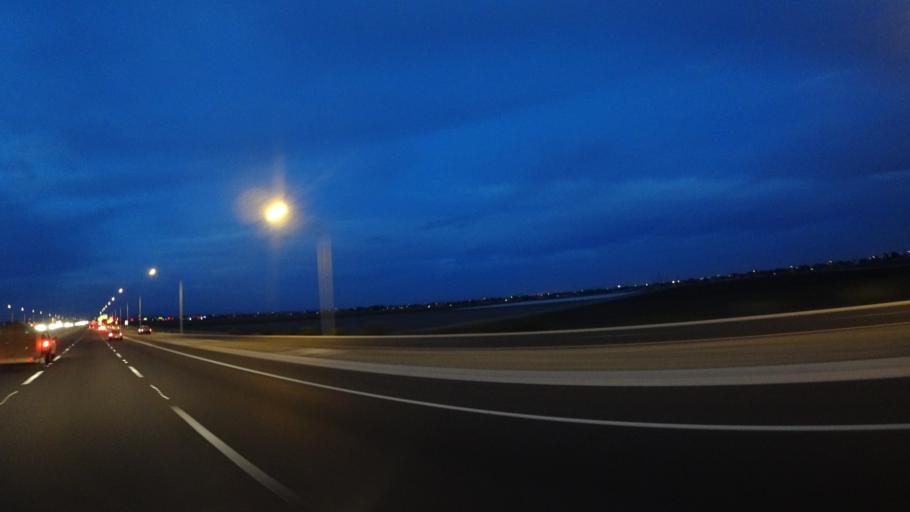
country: US
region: Arizona
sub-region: Maricopa County
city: Citrus Park
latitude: 33.6128
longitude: -112.4179
